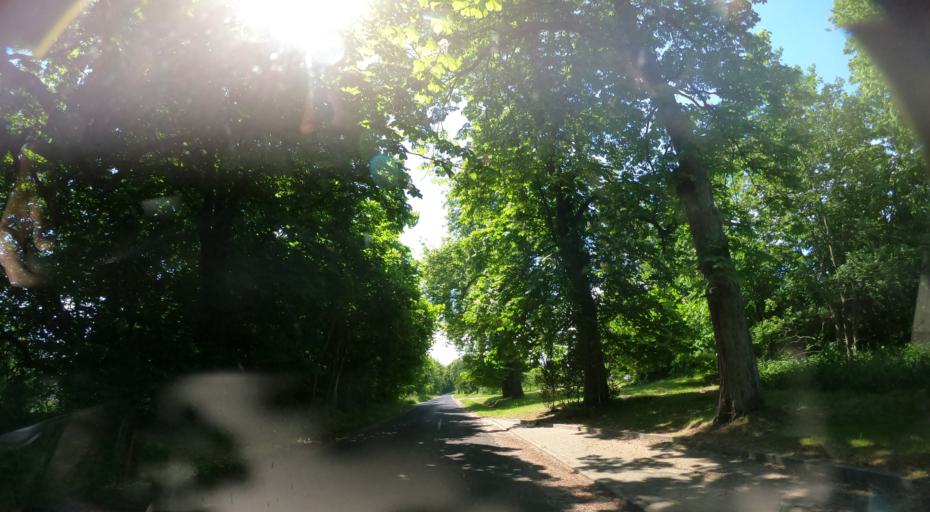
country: PL
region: West Pomeranian Voivodeship
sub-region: Powiat kolobrzeski
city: Ustronie Morskie
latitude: 54.1626
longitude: 15.8095
